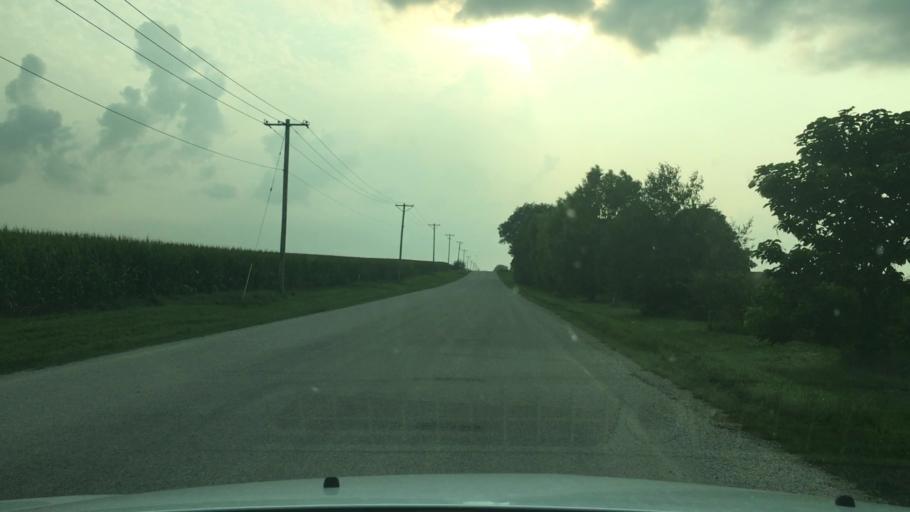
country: US
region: Illinois
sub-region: Ogle County
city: Rochelle
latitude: 41.9203
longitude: -89.0005
